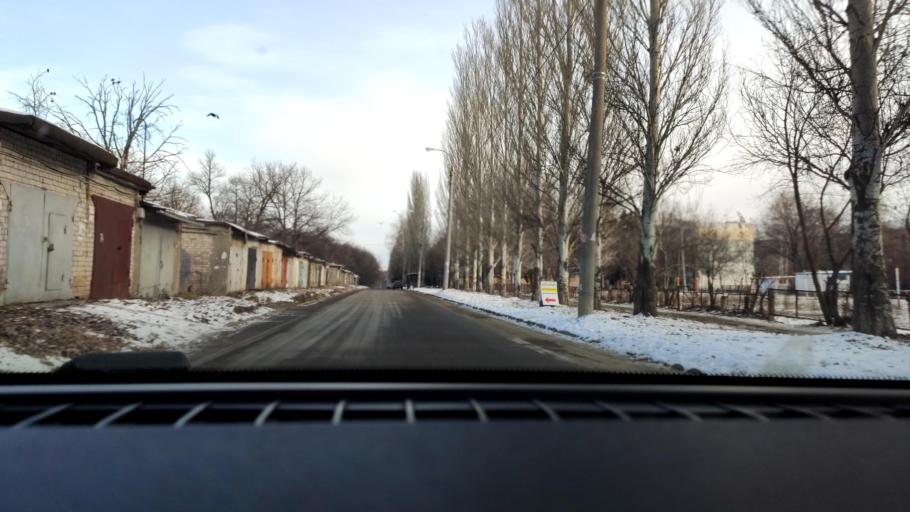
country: RU
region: Samara
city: Petra-Dubrava
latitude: 53.3043
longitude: 50.2699
